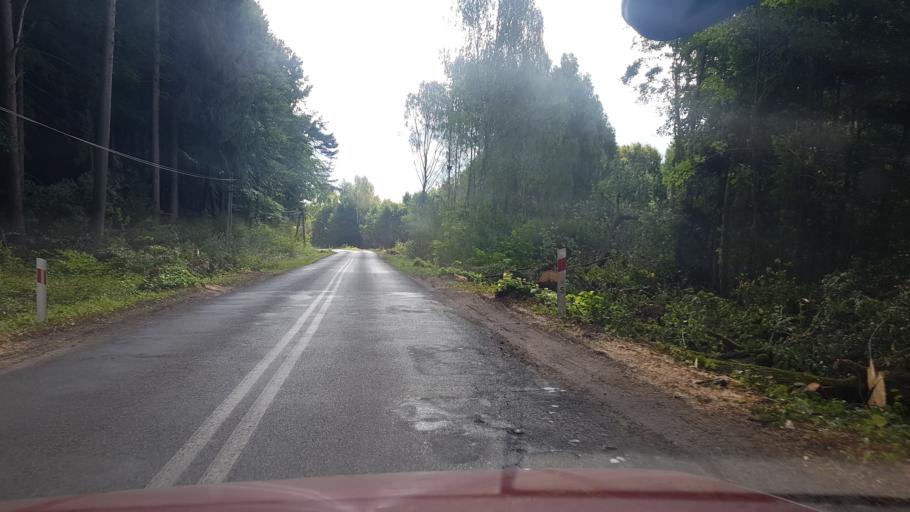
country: PL
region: West Pomeranian Voivodeship
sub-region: Powiat koszalinski
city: Polanow
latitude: 54.1175
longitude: 16.6985
